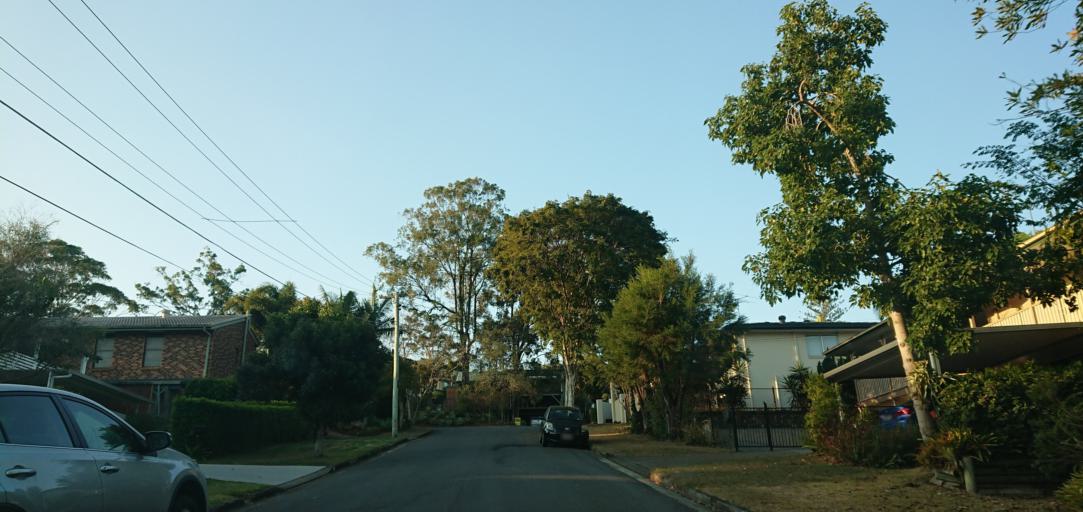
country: AU
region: Queensland
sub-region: Brisbane
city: Kenmore Hills
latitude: -27.5021
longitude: 152.9558
